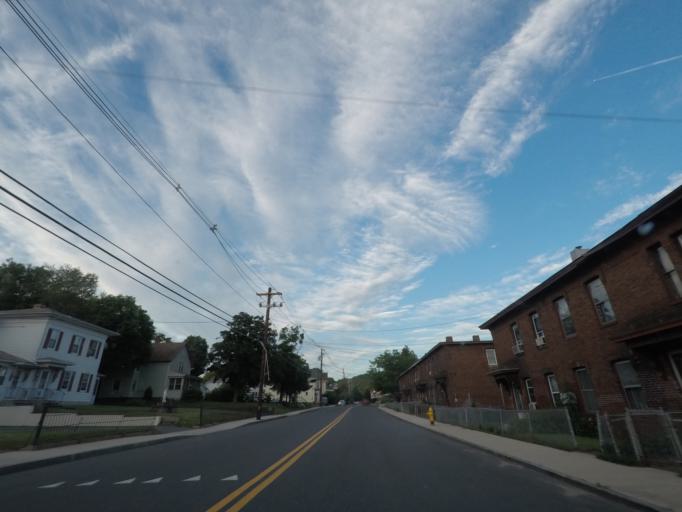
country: US
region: Massachusetts
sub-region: Hampshire County
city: Ware
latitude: 42.2121
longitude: -72.2395
